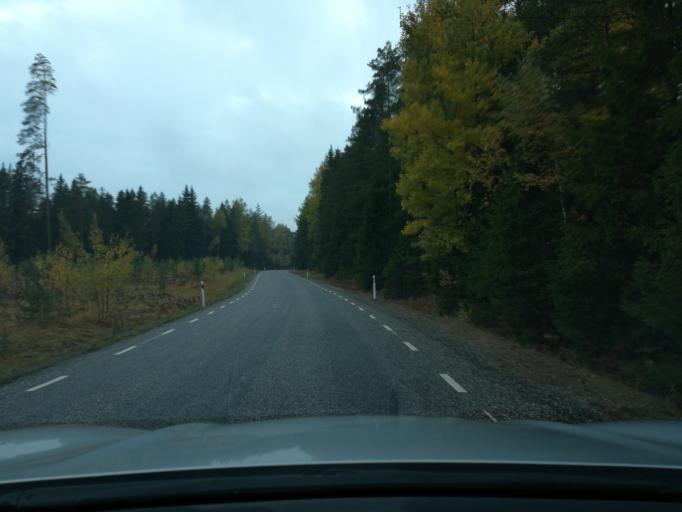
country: EE
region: Ida-Virumaa
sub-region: Johvi vald
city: Johvi
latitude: 59.1682
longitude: 27.4417
